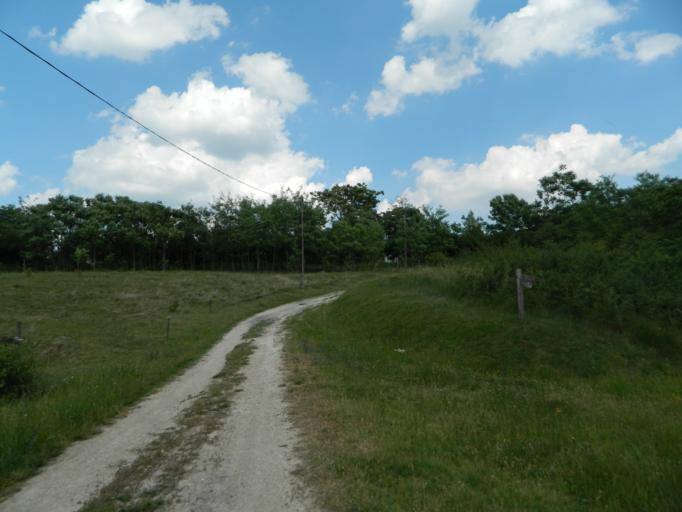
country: HU
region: Somogy
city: Tab
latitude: 46.7793
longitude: 17.9608
